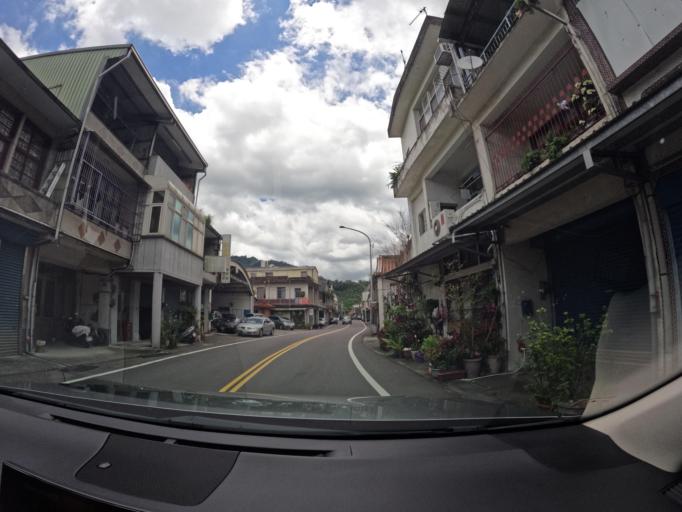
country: TW
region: Taiwan
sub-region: Hsinchu
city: Hsinchu
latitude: 24.6265
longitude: 121.0093
